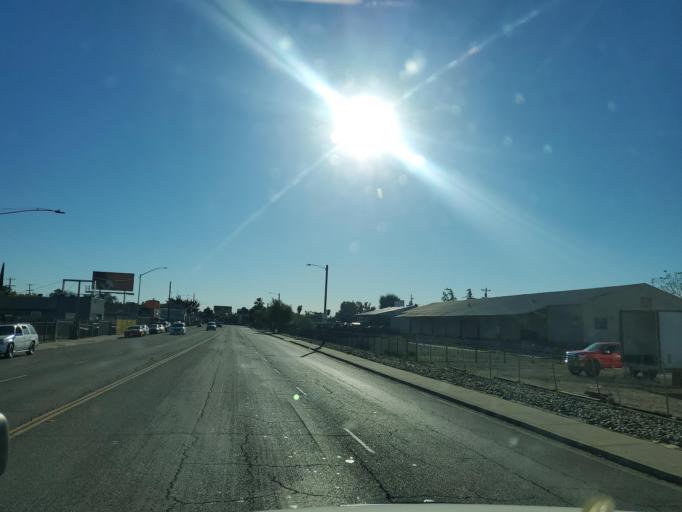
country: US
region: California
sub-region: San Joaquin County
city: August
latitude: 37.9770
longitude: -121.2748
